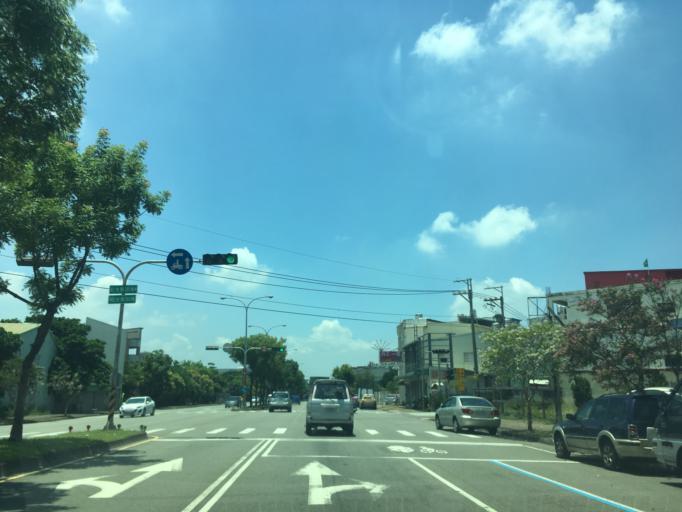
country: TW
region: Taiwan
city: Fengyuan
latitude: 24.2420
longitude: 120.7031
